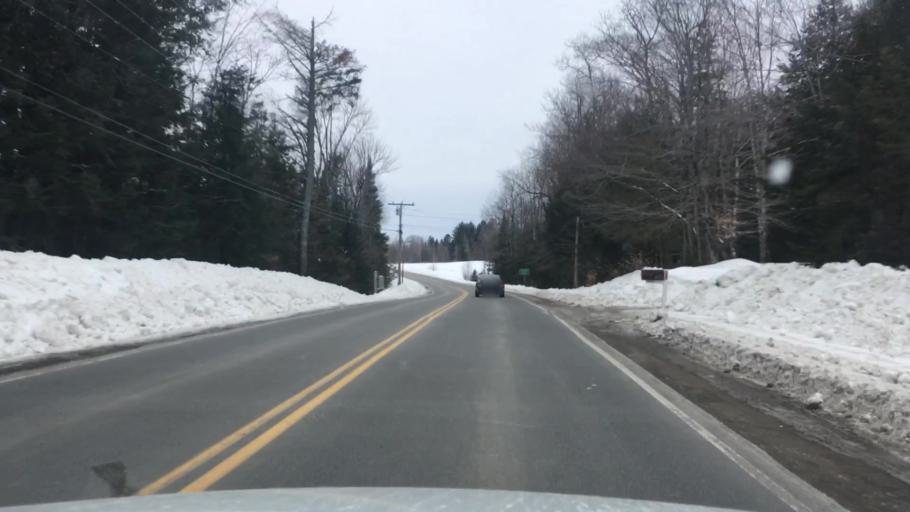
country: US
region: Maine
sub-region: Penobscot County
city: Garland
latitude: 44.9937
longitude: -69.0792
